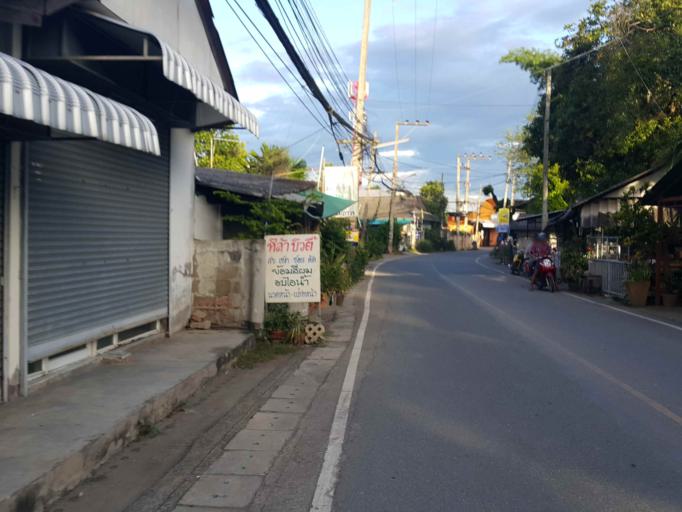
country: TH
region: Chiang Mai
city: Chiang Mai
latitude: 18.7779
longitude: 99.0399
